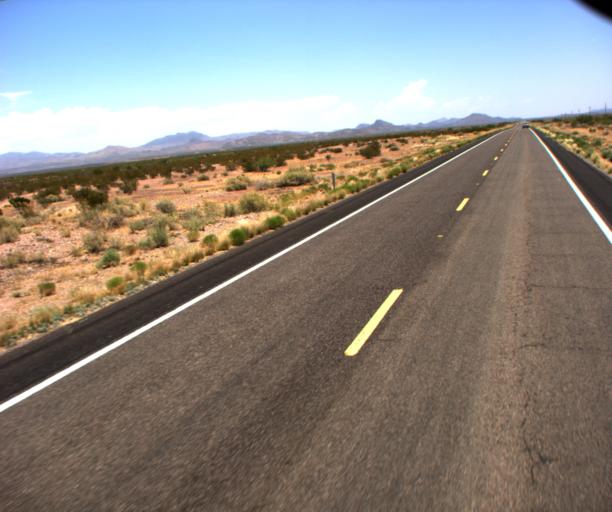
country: US
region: Arizona
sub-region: Graham County
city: Safford
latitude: 32.7792
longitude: -109.5216
